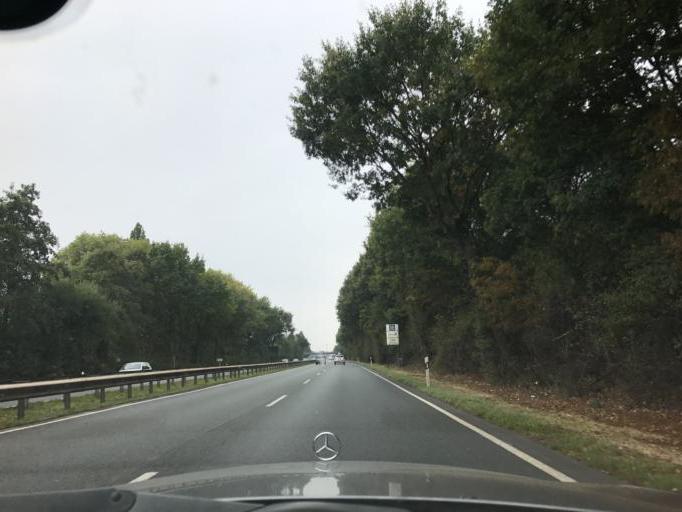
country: DE
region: Bremen
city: Bremen
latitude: 53.0446
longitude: 8.8319
